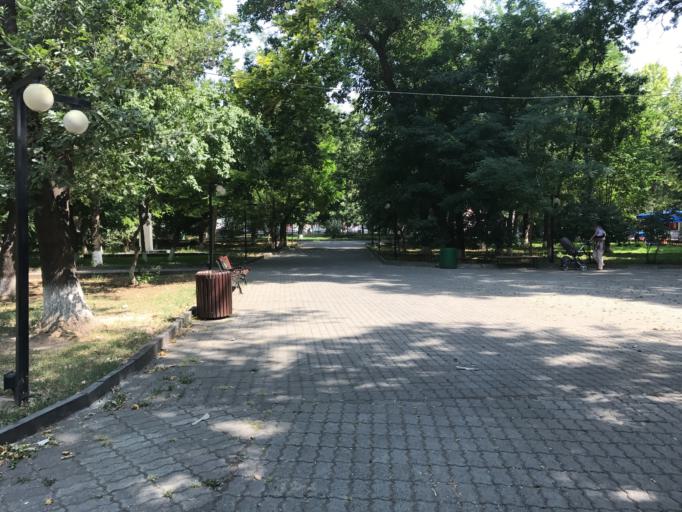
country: AM
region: Yerevan
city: Yerevan
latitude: 40.1758
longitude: 44.5060
